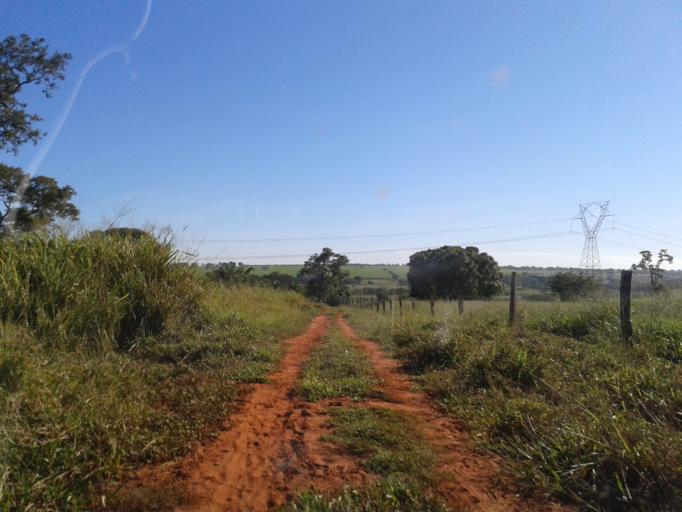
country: BR
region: Minas Gerais
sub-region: Santa Vitoria
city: Santa Vitoria
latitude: -19.0052
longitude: -50.3181
